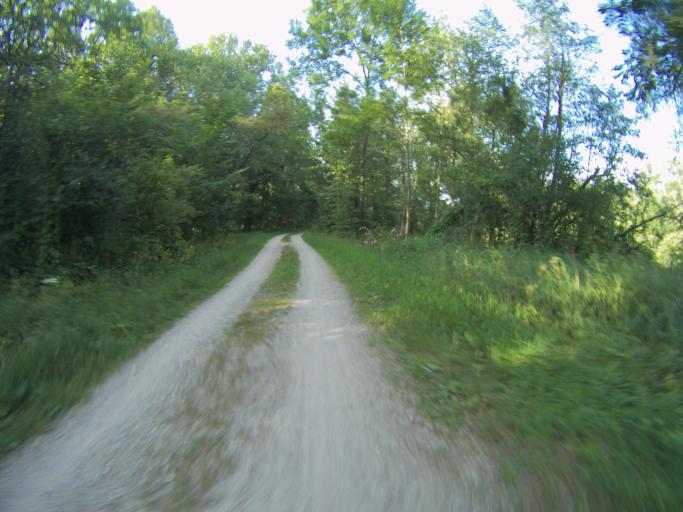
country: DE
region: Bavaria
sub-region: Upper Bavaria
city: Neufahrn bei Freising
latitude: 48.3211
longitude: 11.6991
